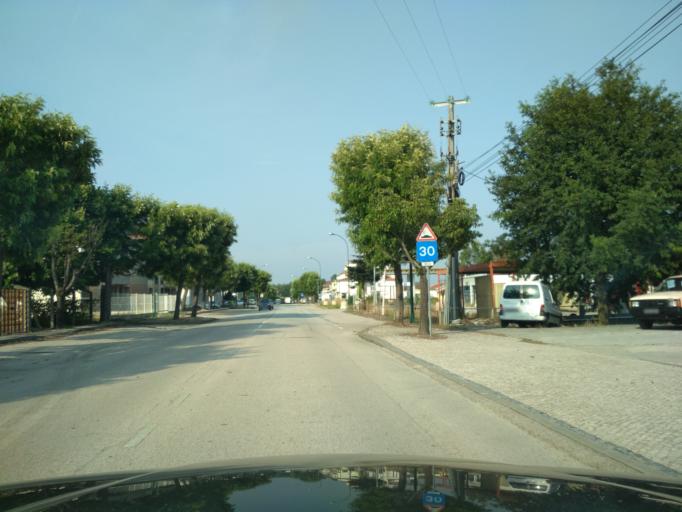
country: PT
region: Viseu
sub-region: Santa Comba Dao
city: Santa Comba Dao
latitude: 40.3893
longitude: -8.1436
